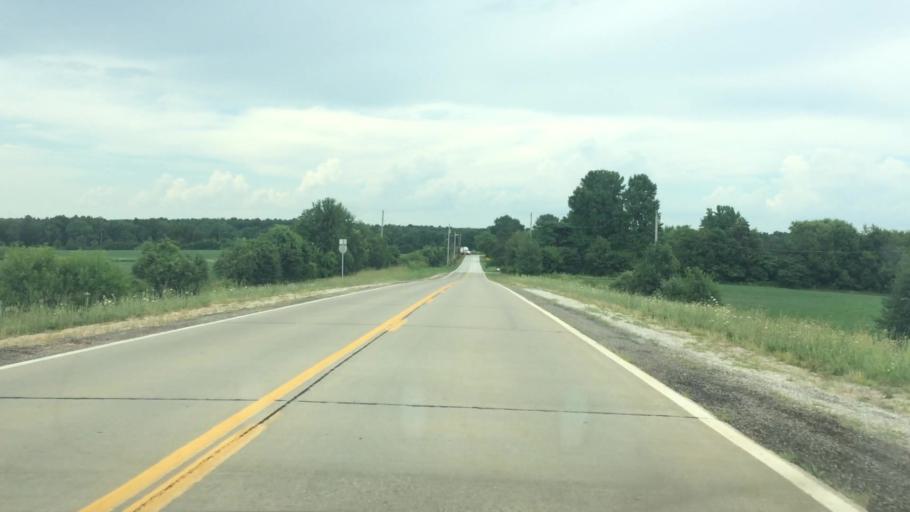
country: US
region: Missouri
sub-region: Greene County
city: Strafford
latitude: 37.2520
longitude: -93.1833
